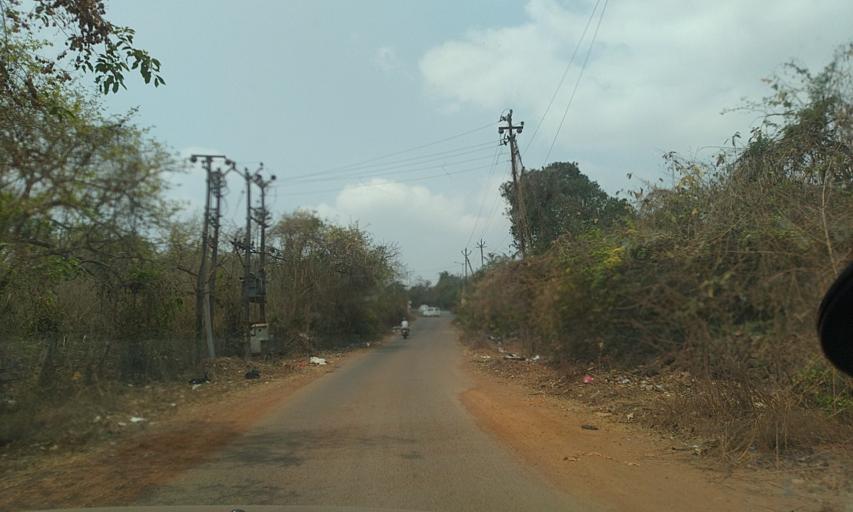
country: IN
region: Goa
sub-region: North Goa
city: Goa Velha
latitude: 15.4920
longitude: 73.9084
